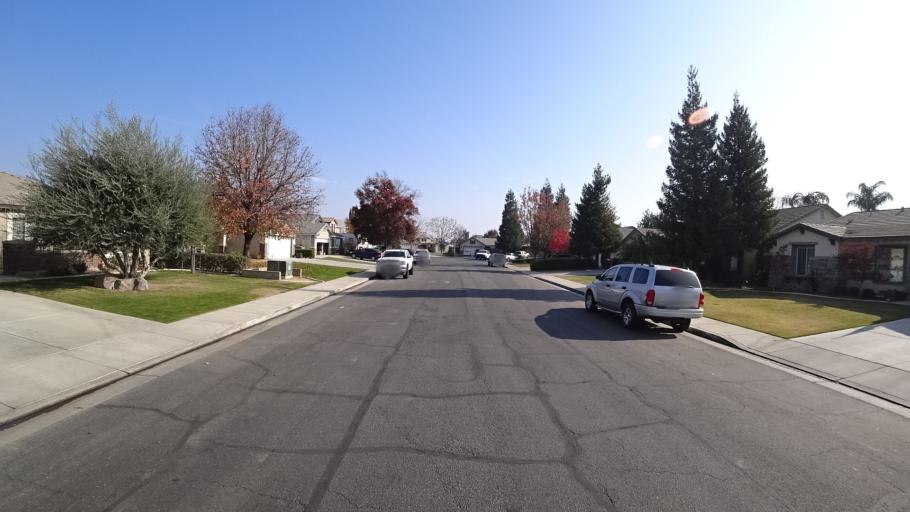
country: US
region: California
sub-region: Kern County
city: Greenacres
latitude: 35.4168
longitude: -119.1259
